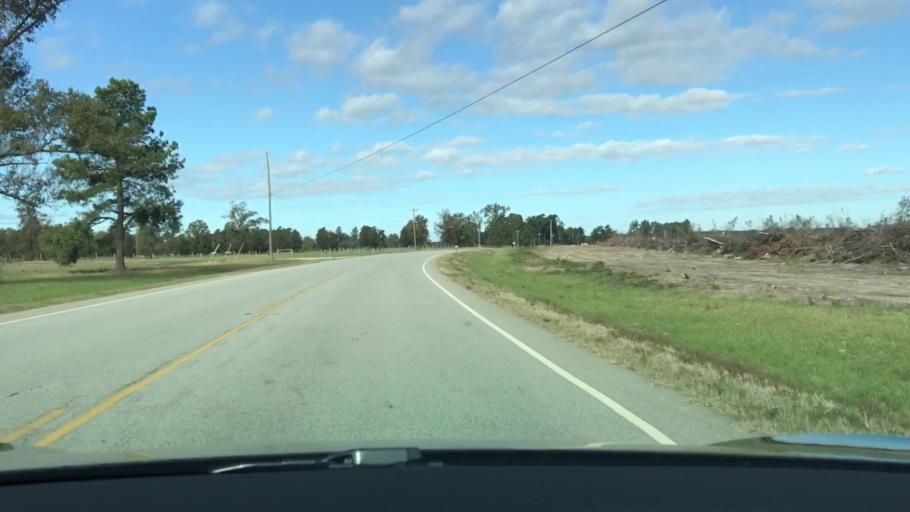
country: US
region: Georgia
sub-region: Jefferson County
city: Wrens
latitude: 33.1182
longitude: -82.4418
